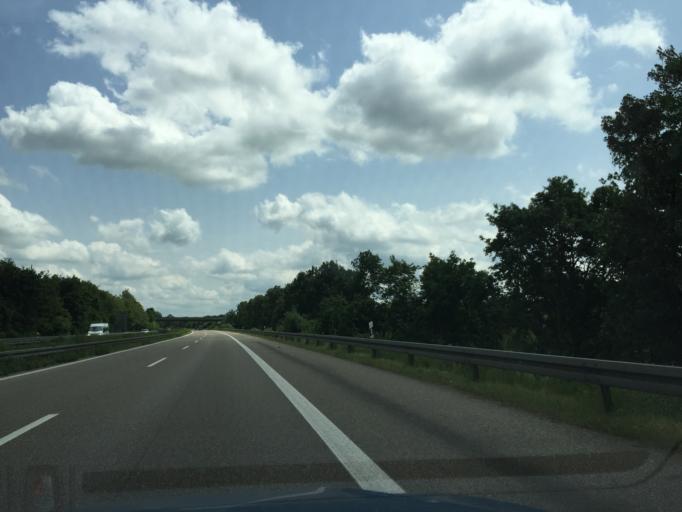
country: DE
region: Bavaria
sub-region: Swabia
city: Senden
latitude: 48.3336
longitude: 10.0438
